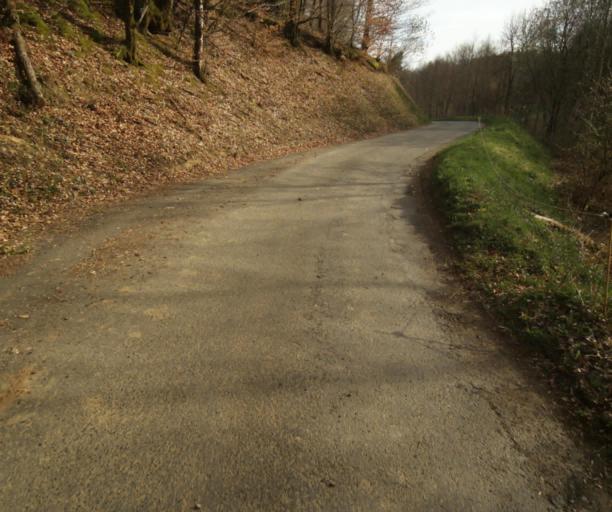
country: FR
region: Limousin
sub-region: Departement de la Correze
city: Naves
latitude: 45.2987
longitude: 1.7550
